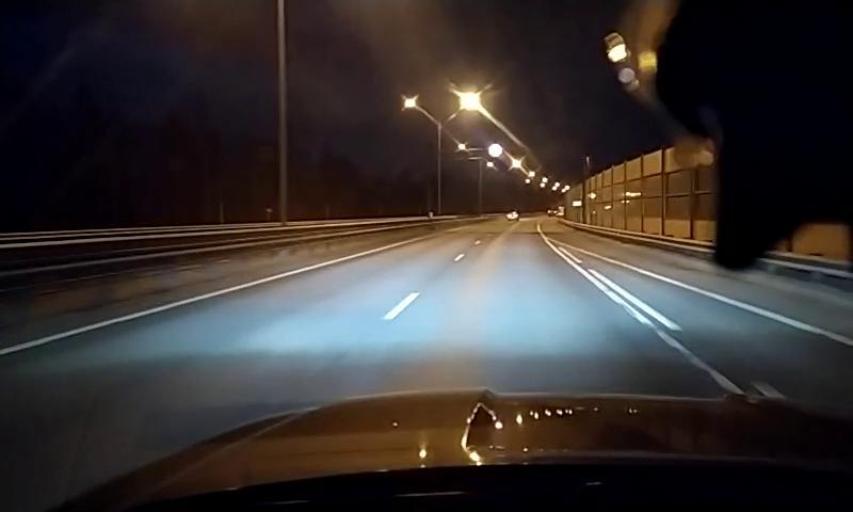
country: RU
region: Leningrad
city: Agalatovo
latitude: 60.2357
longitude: 30.3569
